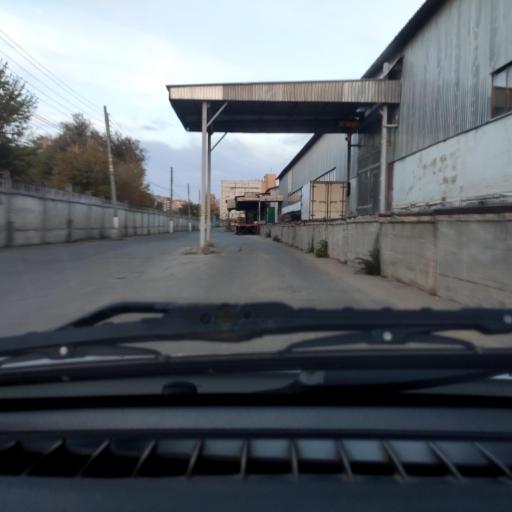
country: RU
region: Samara
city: Zhigulevsk
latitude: 53.4818
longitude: 49.4908
